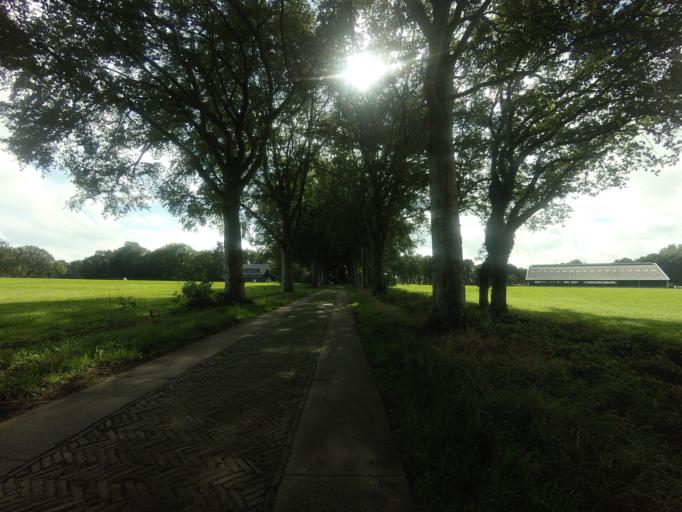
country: NL
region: Friesland
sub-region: Gemeente Heerenveen
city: Jubbega
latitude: 53.0099
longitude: 6.2882
